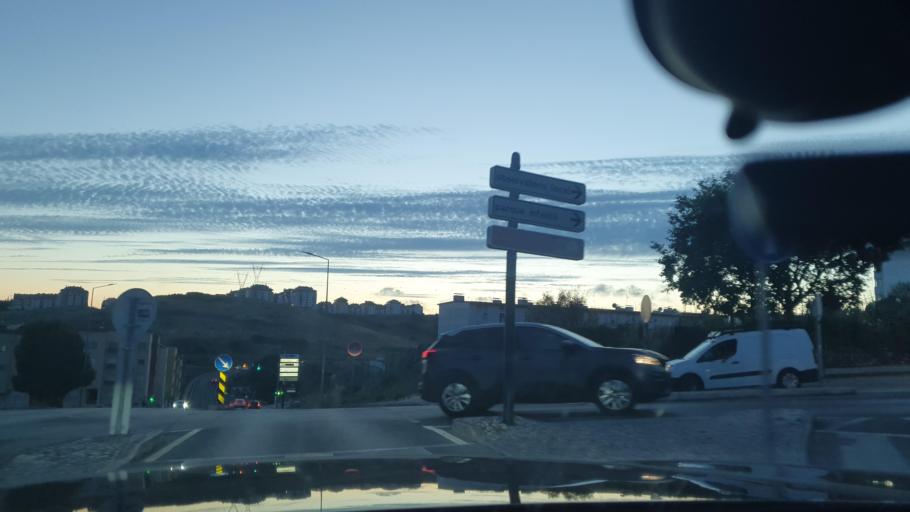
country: PT
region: Lisbon
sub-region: Sintra
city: Queluz
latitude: 38.7617
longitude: -9.2660
